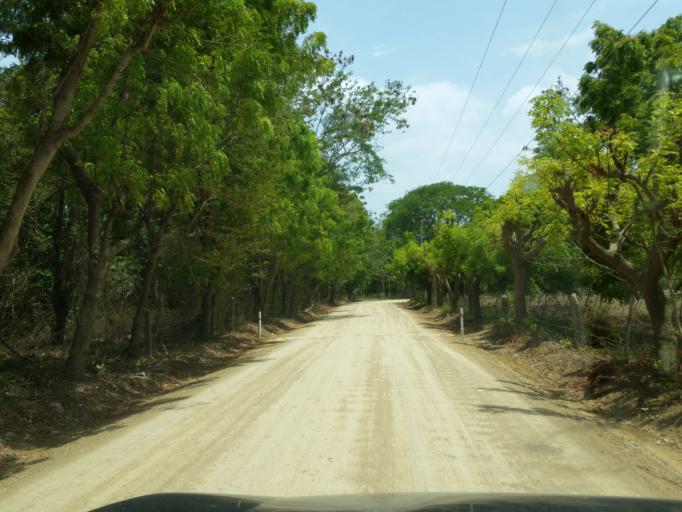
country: NI
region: Rivas
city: Tola
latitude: 11.4225
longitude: -86.0322
